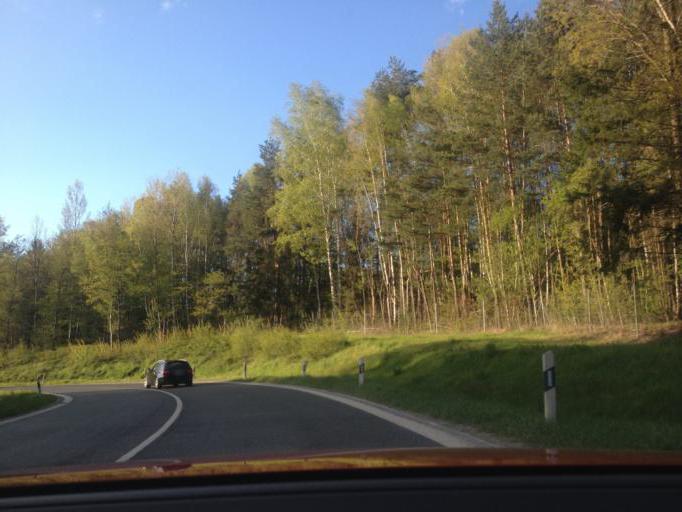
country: DE
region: Bavaria
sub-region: Regierungsbezirk Mittelfranken
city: Feucht
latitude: 49.4065
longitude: 11.1973
